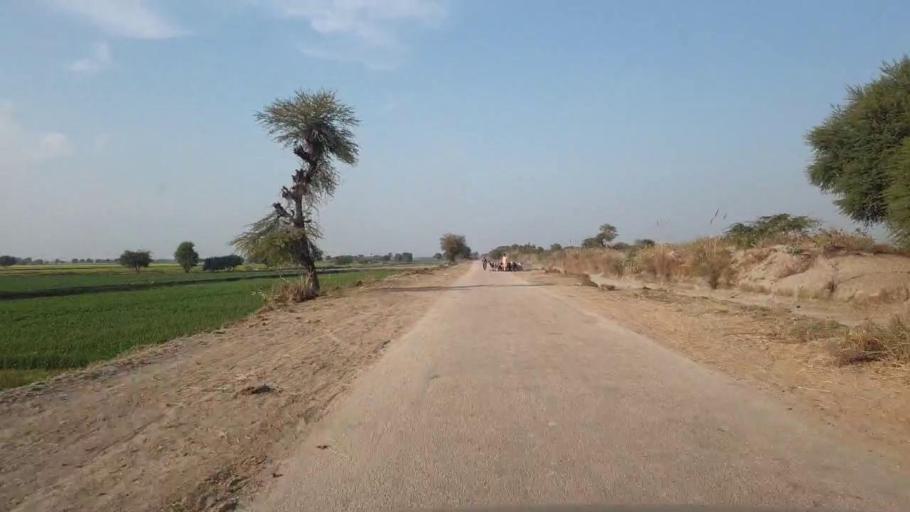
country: PK
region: Sindh
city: Shahpur Chakar
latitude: 26.1639
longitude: 68.6405
